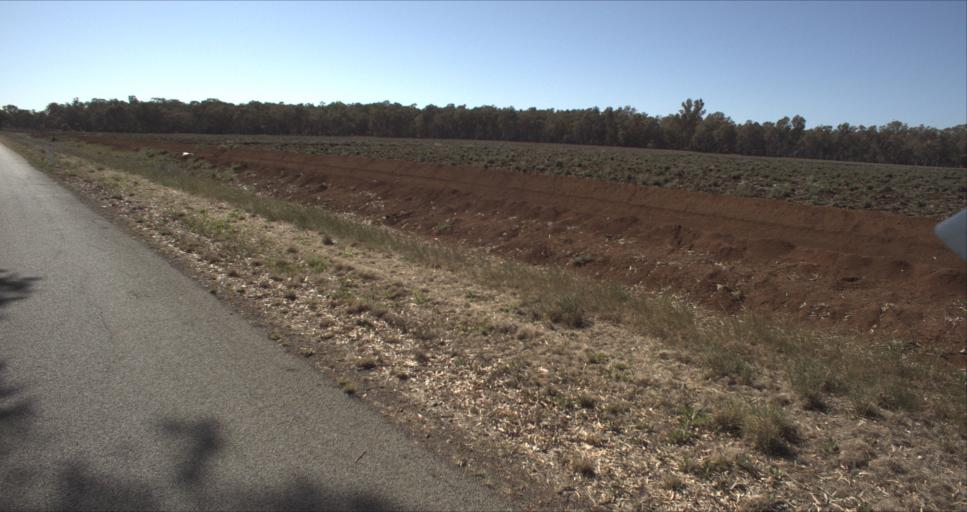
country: AU
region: New South Wales
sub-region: Leeton
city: Leeton
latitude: -34.6059
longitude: 146.2586
